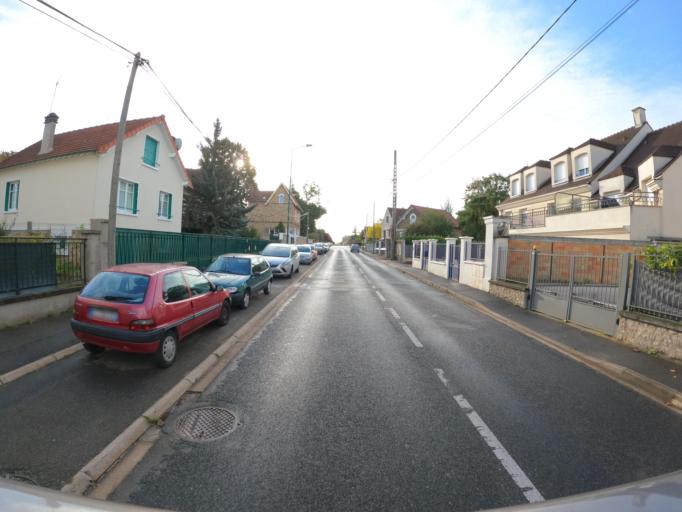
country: FR
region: Ile-de-France
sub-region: Departement de Seine-et-Marne
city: Brou-sur-Chantereine
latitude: 48.8804
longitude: 2.6343
